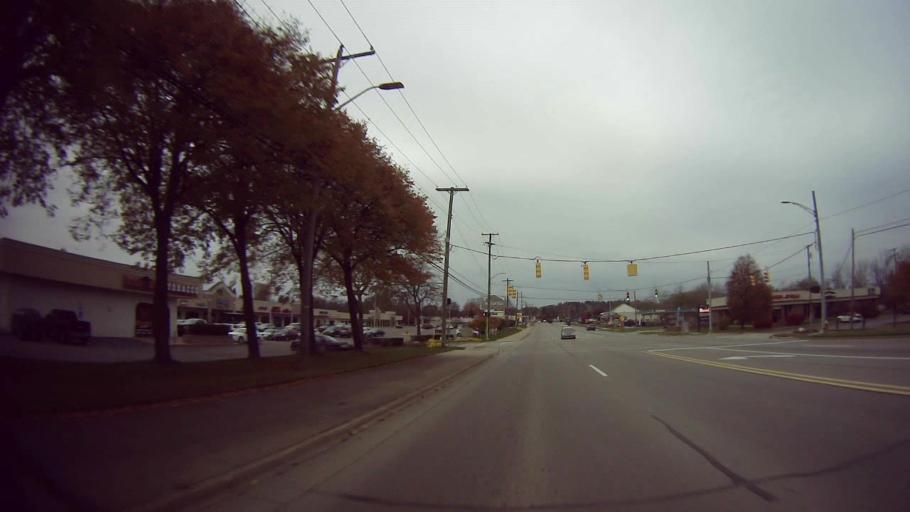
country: US
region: Michigan
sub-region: Oakland County
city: Waterford
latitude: 42.7015
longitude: -83.4022
